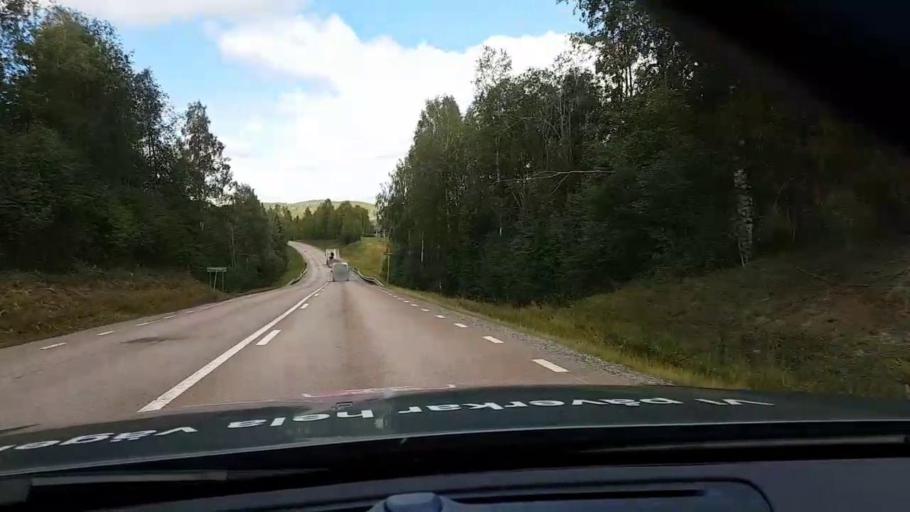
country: SE
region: Vaesternorrland
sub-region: OErnskoeldsviks Kommun
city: Bjasta
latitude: 63.3717
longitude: 18.4370
